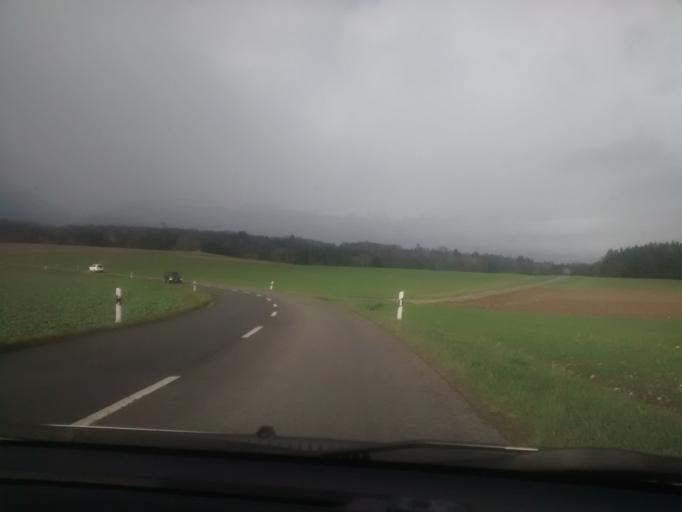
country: CH
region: Vaud
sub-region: Jura-Nord vaudois District
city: Montagny
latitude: 46.7926
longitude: 6.5962
